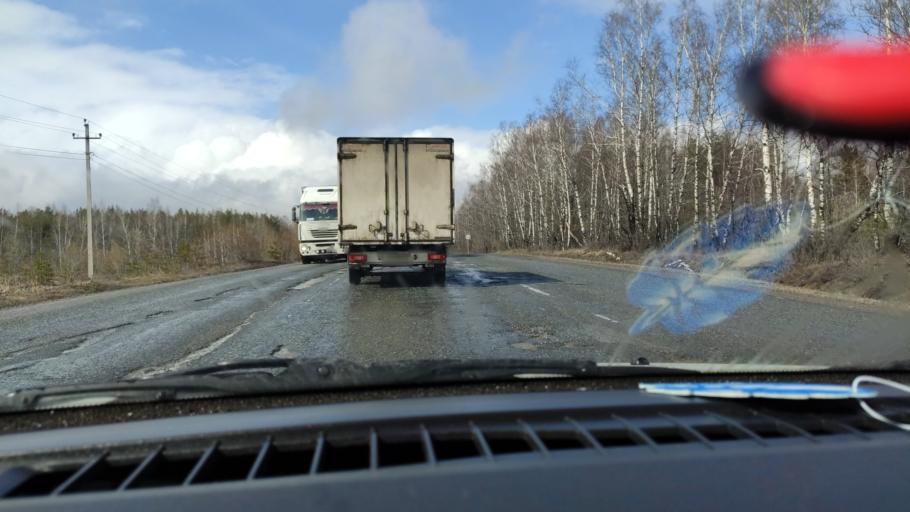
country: RU
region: Perm
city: Suksun
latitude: 57.0870
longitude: 57.3971
